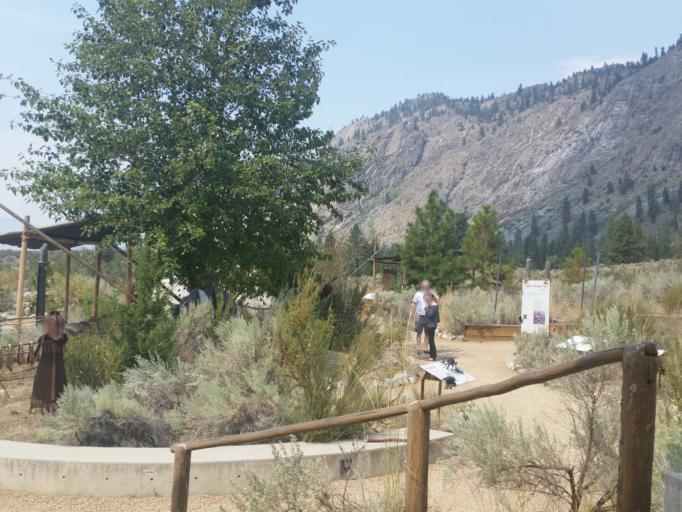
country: CA
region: British Columbia
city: Osoyoos
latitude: 49.0418
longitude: -119.4339
